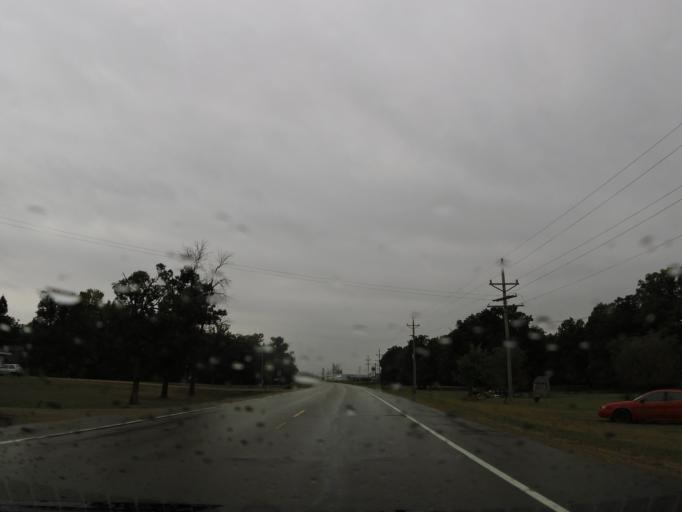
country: US
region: Minnesota
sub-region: Marshall County
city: Warren
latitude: 48.4431
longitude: -96.8675
